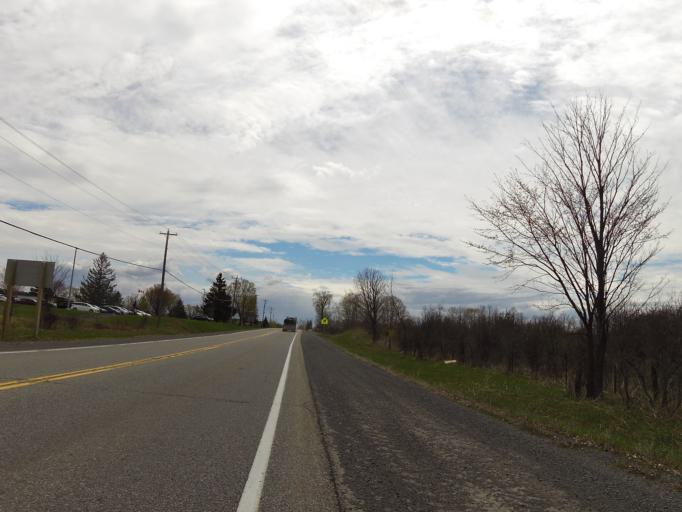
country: CA
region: Ontario
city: Hawkesbury
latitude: 45.5496
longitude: -74.6365
